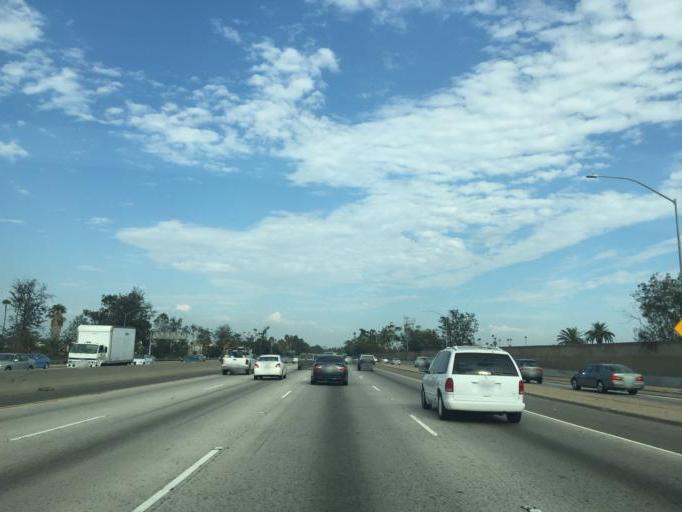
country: US
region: California
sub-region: Los Angeles County
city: View Park-Windsor Hills
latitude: 34.0342
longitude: -118.3487
